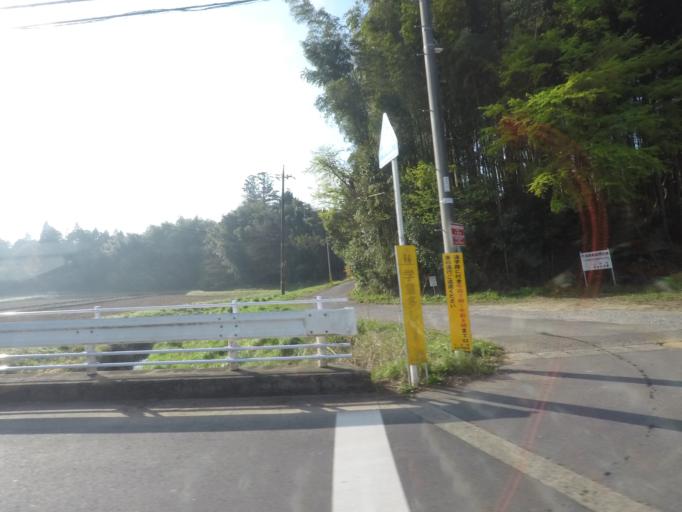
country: JP
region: Chiba
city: Yachimata
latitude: 35.6364
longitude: 140.2826
